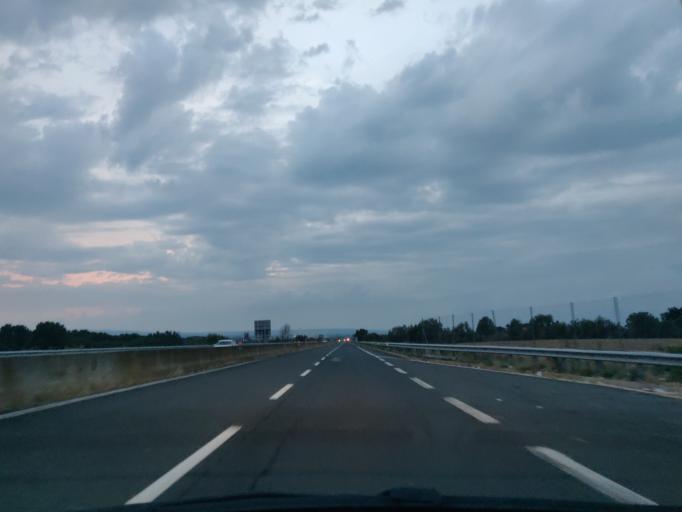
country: IT
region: Latium
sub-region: Provincia di Viterbo
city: Vetralla
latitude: 42.3711
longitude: 12.0443
